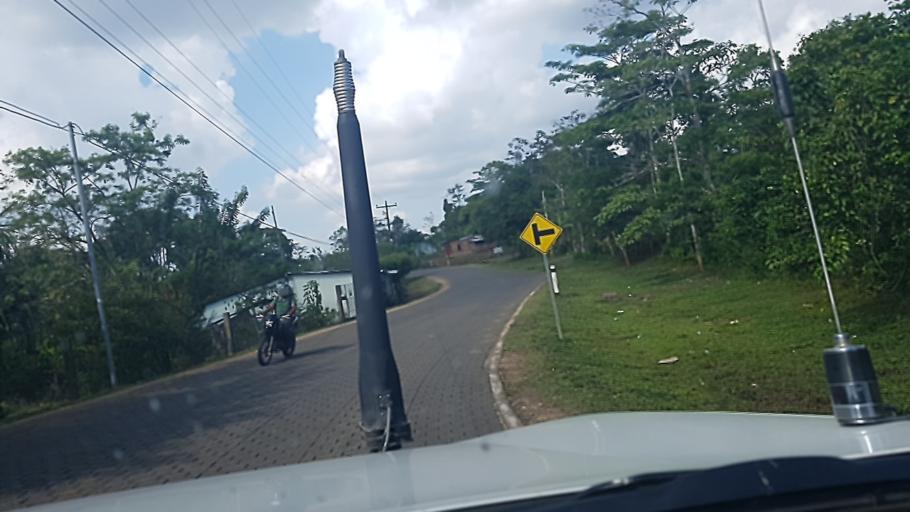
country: NI
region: Atlantico Sur
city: Nueva Guinea
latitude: 11.7032
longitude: -84.3767
